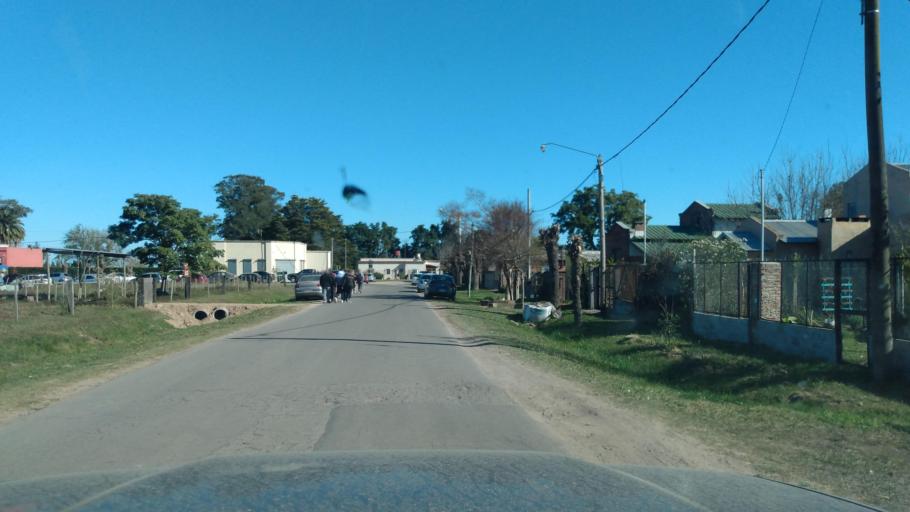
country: AR
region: Buenos Aires
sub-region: Partido de Lujan
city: Lujan
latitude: -34.4848
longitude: -59.2225
